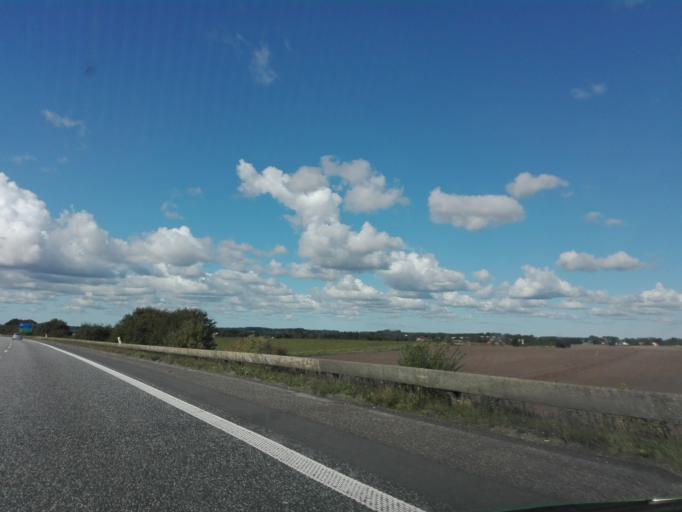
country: DK
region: Central Jutland
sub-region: Randers Kommune
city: Spentrup
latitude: 56.5342
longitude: 9.9253
